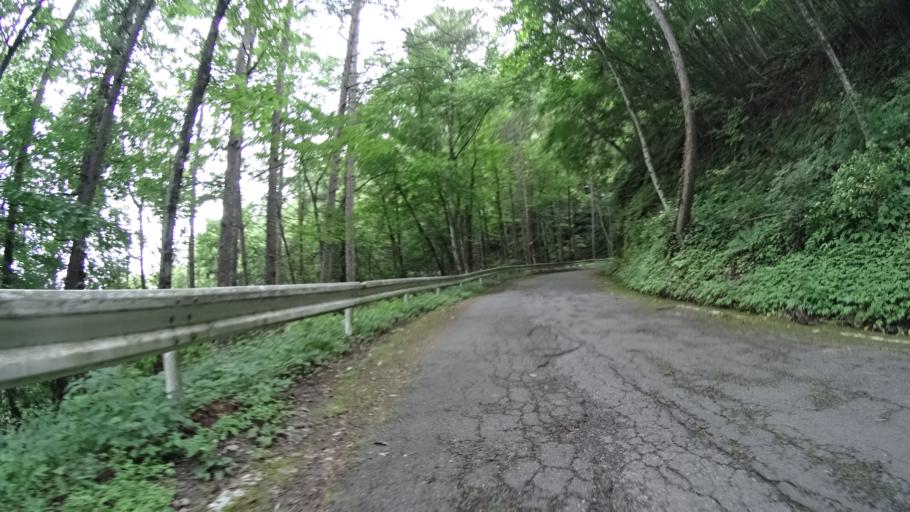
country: JP
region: Nagano
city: Saku
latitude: 36.0722
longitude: 138.6447
